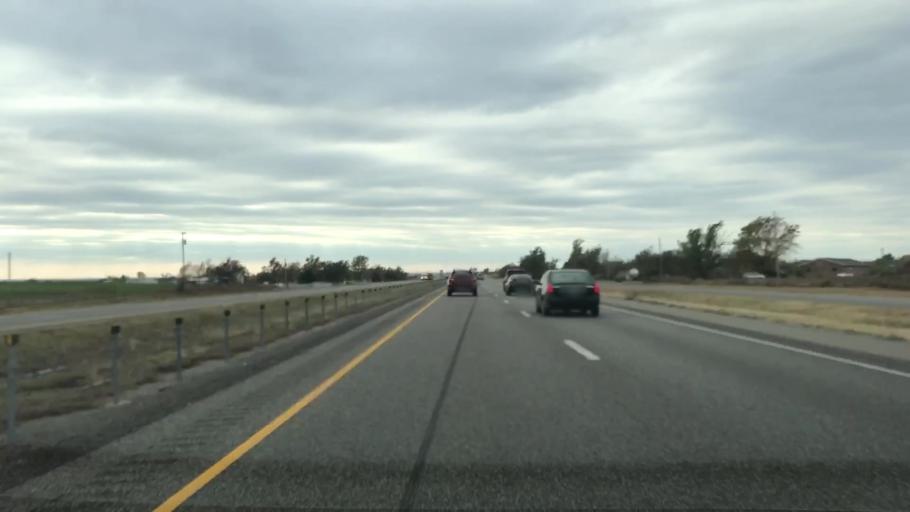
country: US
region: Oklahoma
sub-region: Beckham County
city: Elk City
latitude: 35.3757
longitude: -99.5303
